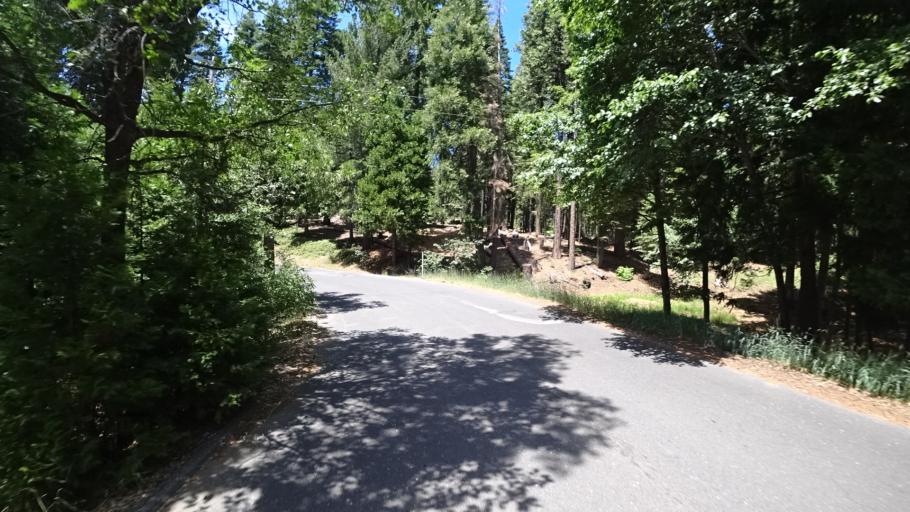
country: US
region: California
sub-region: Calaveras County
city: Arnold
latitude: 38.2985
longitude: -120.2642
